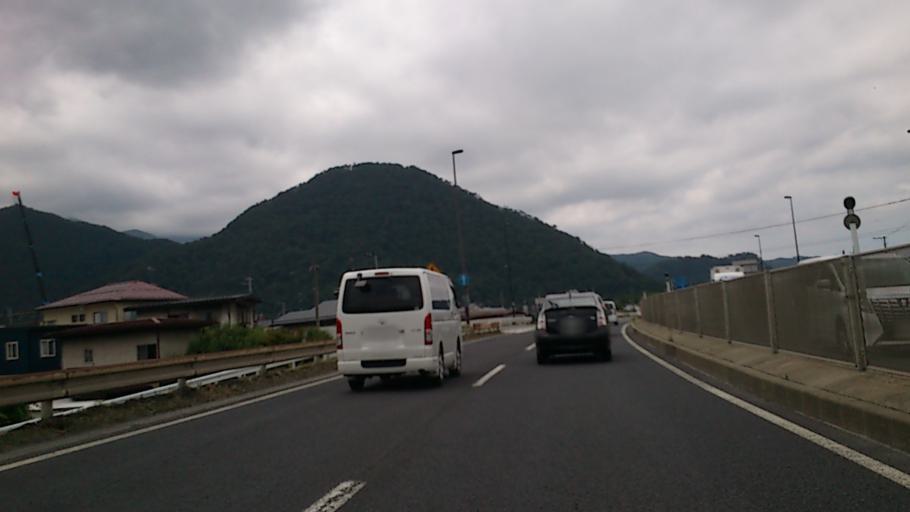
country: JP
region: Yamagata
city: Yamagata-shi
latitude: 38.2479
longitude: 140.3567
